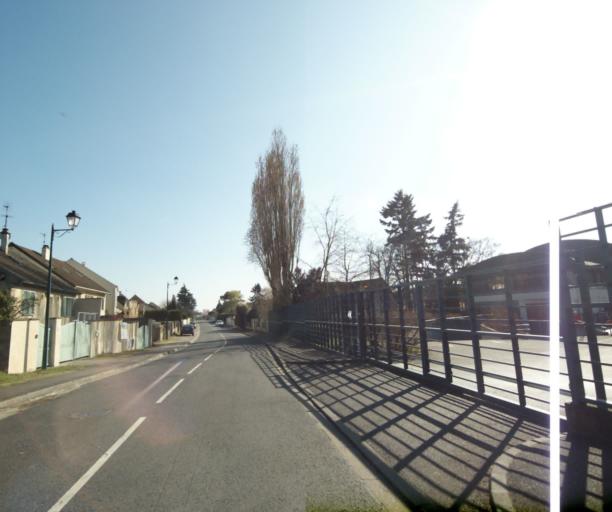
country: FR
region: Ile-de-France
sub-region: Departement du Val-d'Oise
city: Neuville-sur-Oise
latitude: 49.0216
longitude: 2.0559
